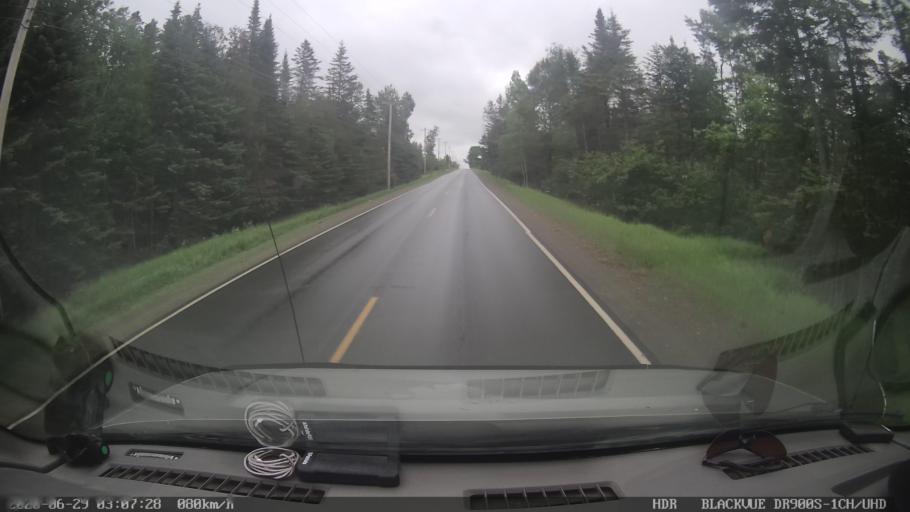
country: US
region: Maine
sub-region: Penobscot County
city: Patten
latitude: 45.8758
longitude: -68.4694
